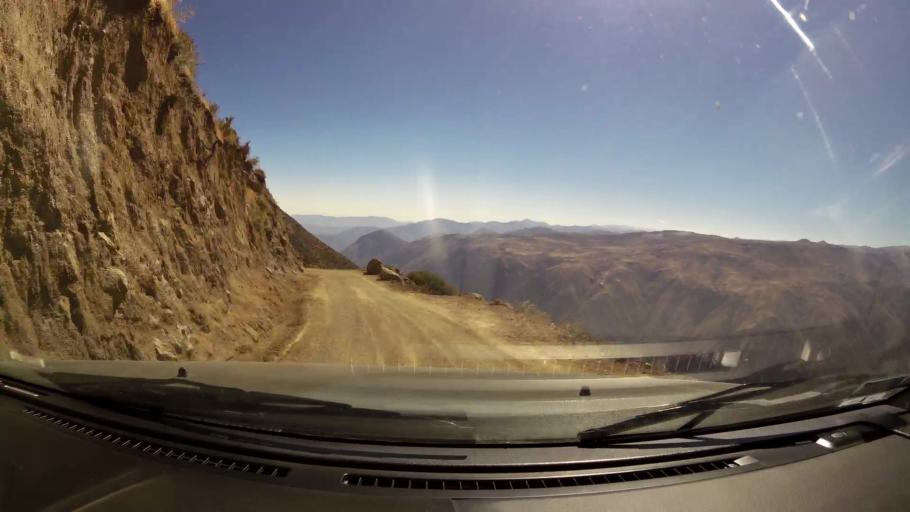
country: PE
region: Huancavelica
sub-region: Huaytara
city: Quito-Arma
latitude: -13.6234
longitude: -75.3537
